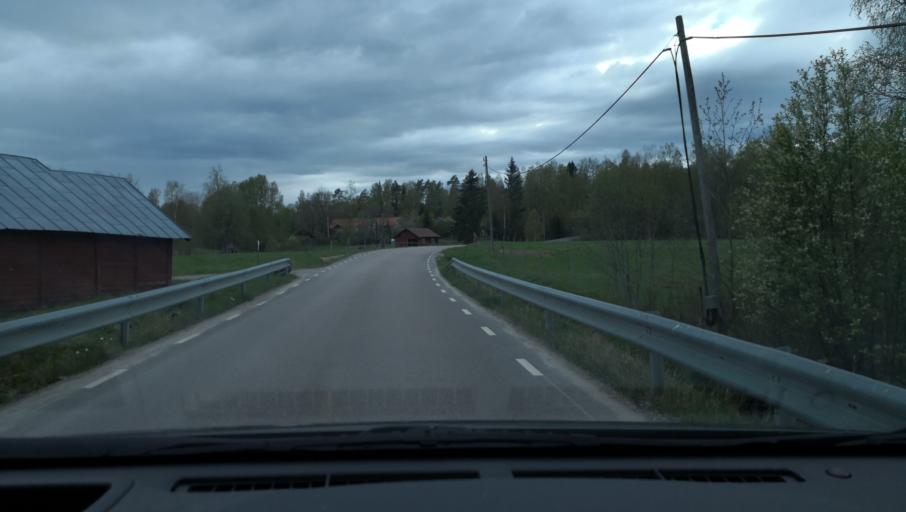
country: SE
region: Vaestmanland
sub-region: Norbergs Kommun
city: Norberg
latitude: 60.0904
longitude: 15.9014
